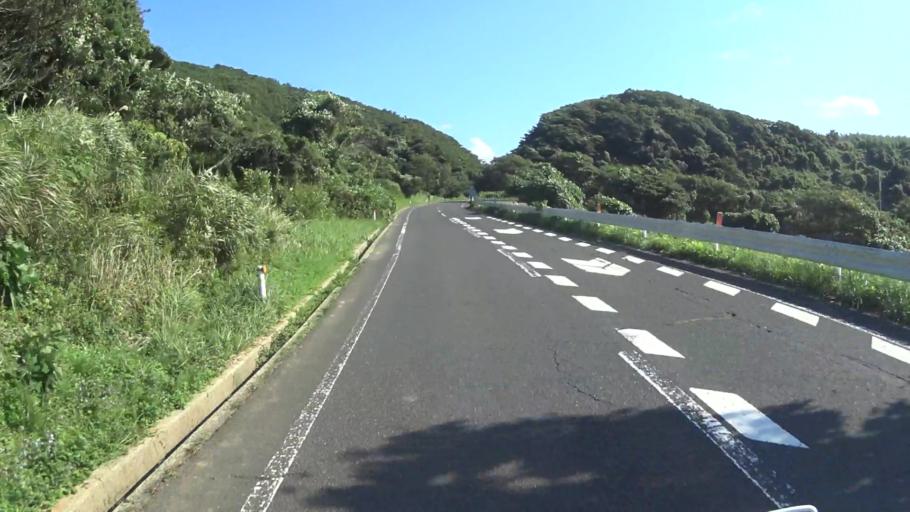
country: JP
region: Kyoto
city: Miyazu
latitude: 35.7145
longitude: 135.0677
